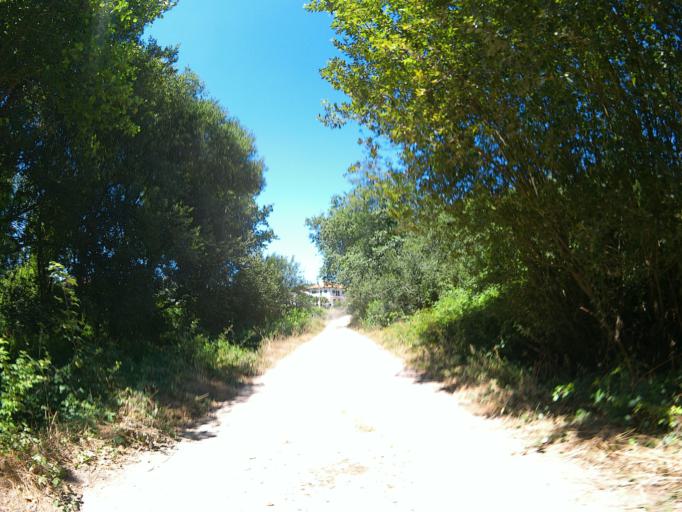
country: PT
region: Viana do Castelo
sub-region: Viana do Castelo
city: Darque
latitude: 41.7149
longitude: -8.7131
